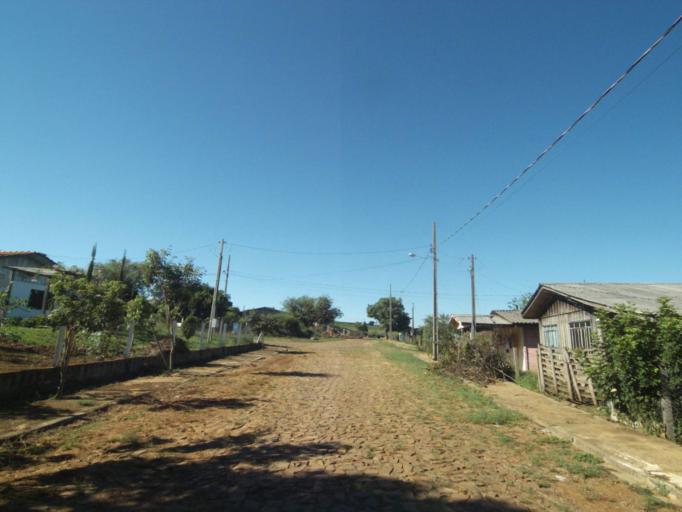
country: BR
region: Parana
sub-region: Pinhao
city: Pinhao
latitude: -25.8419
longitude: -52.0323
